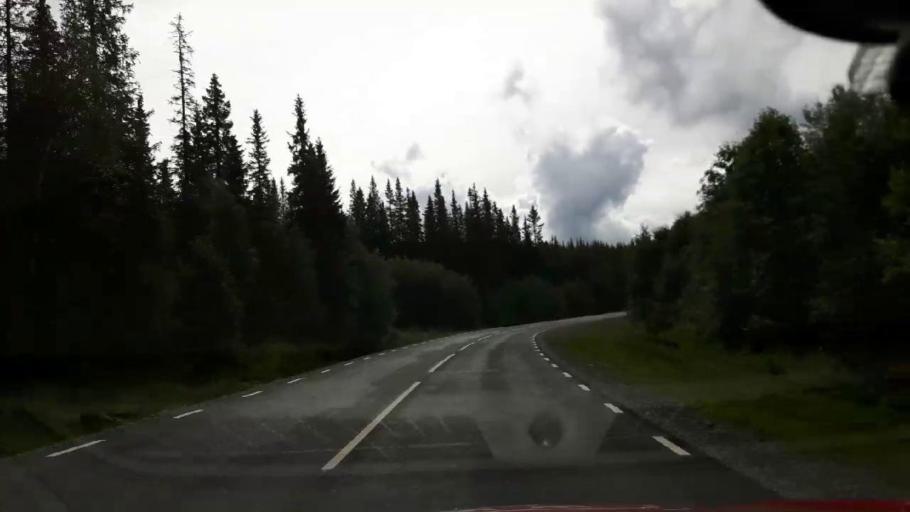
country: NO
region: Nord-Trondelag
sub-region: Lierne
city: Sandvika
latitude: 64.6429
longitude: 14.1418
